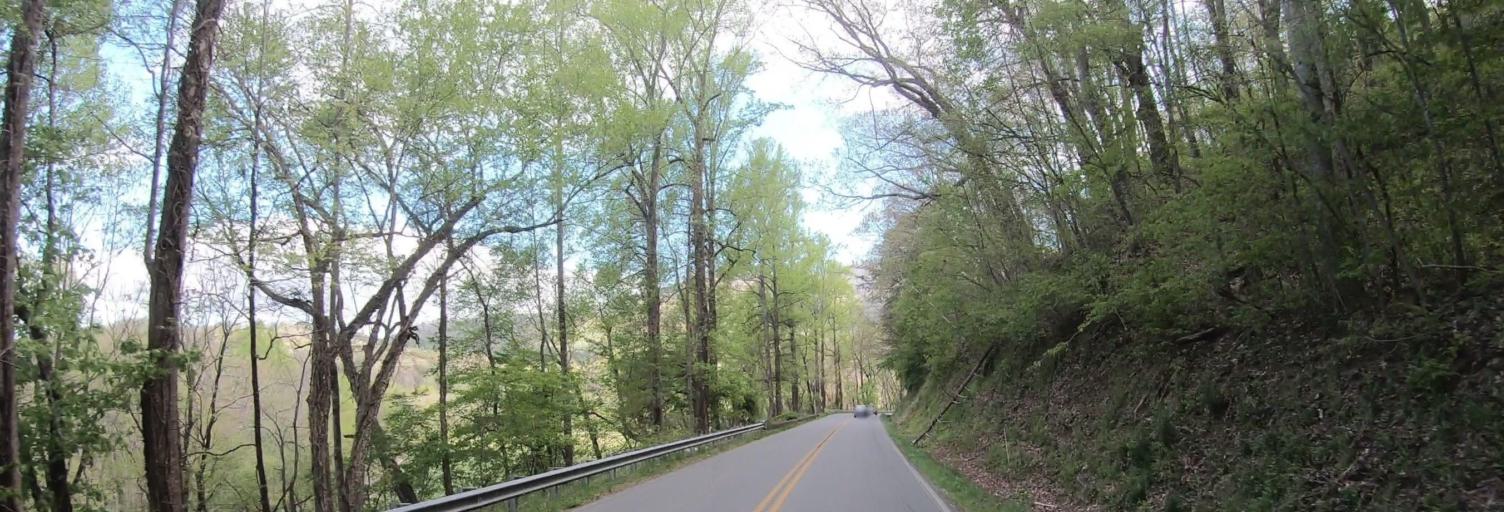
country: US
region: North Carolina
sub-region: Swain County
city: Bryson City
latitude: 35.4455
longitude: -83.4002
